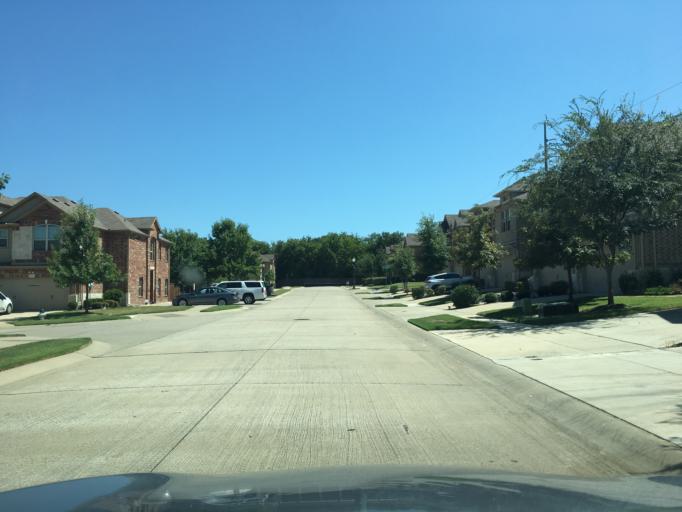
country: US
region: Texas
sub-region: Dallas County
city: Sachse
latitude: 32.9518
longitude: -96.6246
